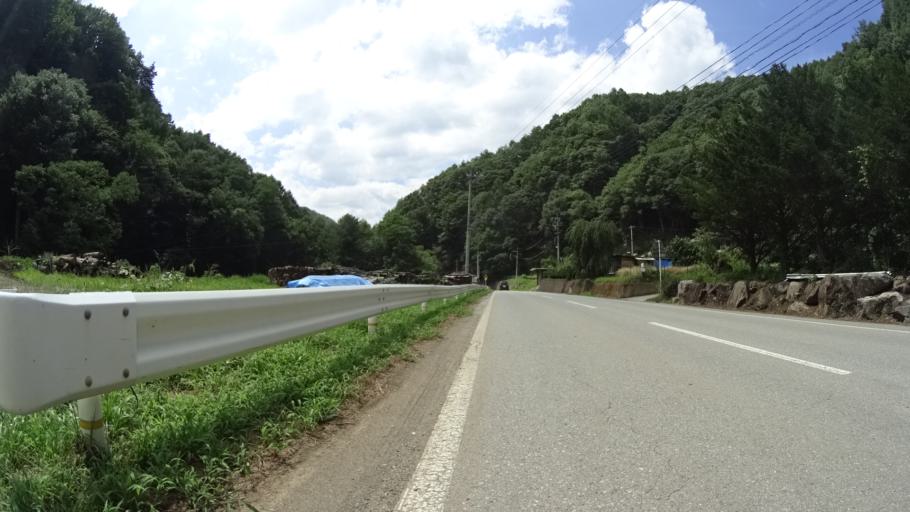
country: JP
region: Nagano
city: Saku
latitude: 36.0612
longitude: 138.5175
